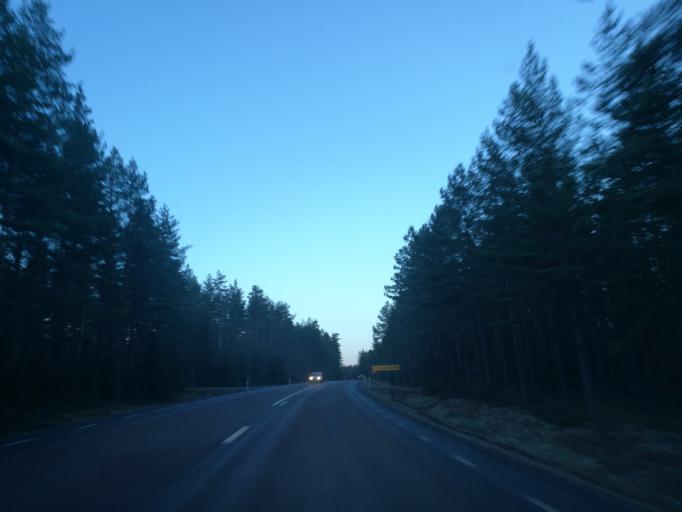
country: SE
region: Vaermland
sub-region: Eda Kommun
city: Charlottenberg
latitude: 59.8976
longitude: 12.2787
